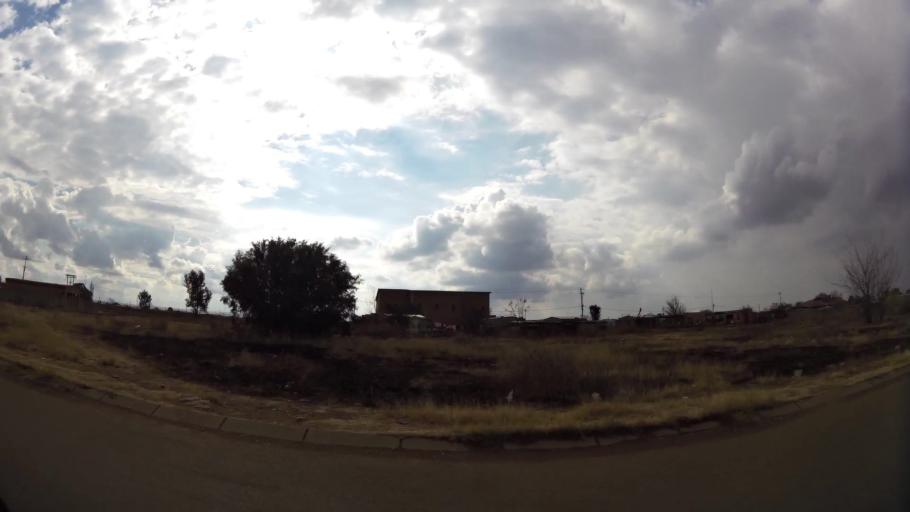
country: ZA
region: Gauteng
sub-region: Sedibeng District Municipality
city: Vanderbijlpark
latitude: -26.7007
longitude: 27.7928
